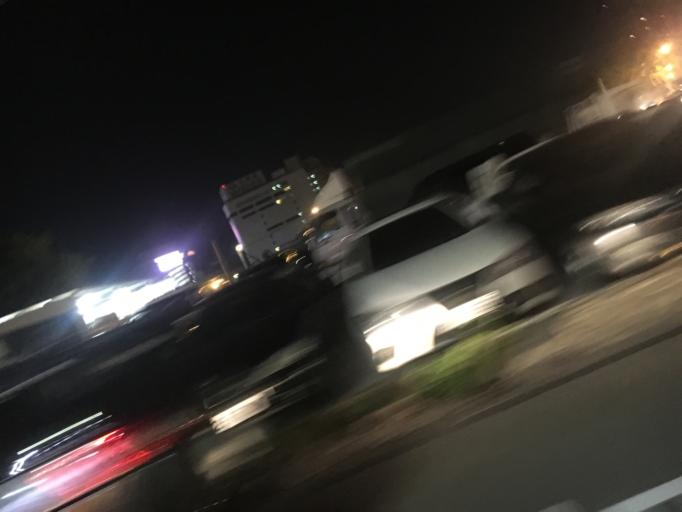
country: TW
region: Taiwan
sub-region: Hsinchu
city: Hsinchu
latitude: 24.8003
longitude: 120.9740
